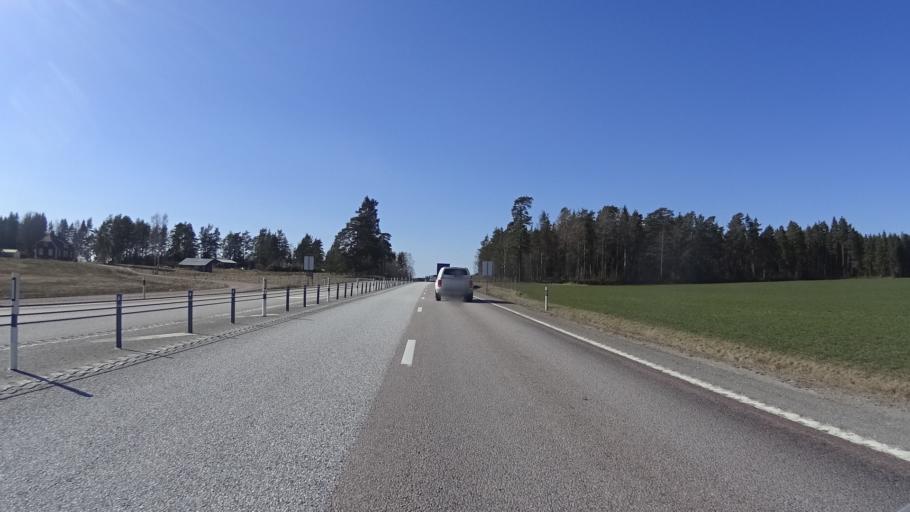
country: SE
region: Vaermland
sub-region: Kristinehamns Kommun
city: Kristinehamn
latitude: 59.3756
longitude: 13.9318
